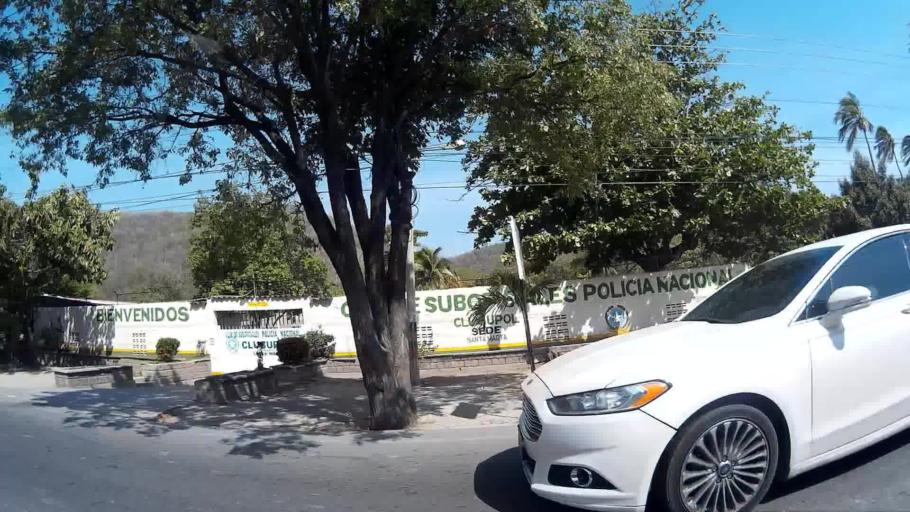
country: CO
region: Magdalena
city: Santa Marta
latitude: 11.1838
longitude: -74.2255
